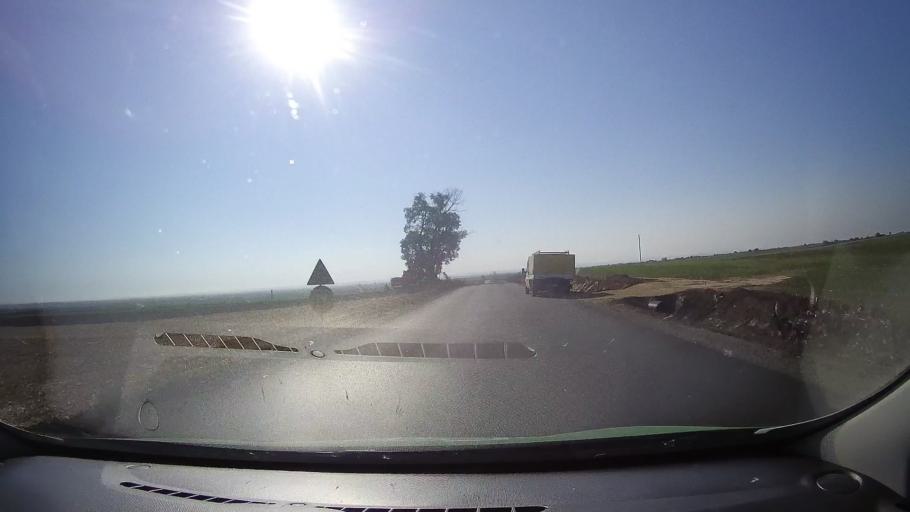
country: RO
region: Satu Mare
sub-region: Comuna Tiream
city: Tiream
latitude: 47.6406
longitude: 22.4652
